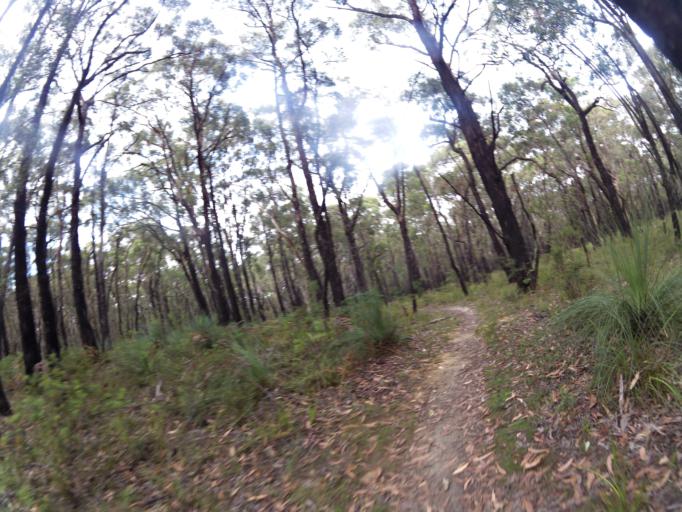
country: AU
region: Victoria
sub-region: Colac-Otway
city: Colac
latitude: -38.4967
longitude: 143.7123
